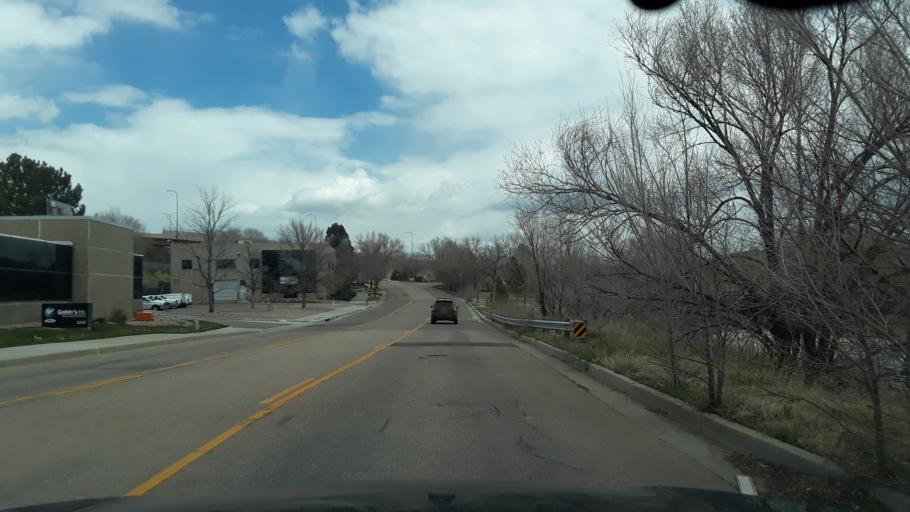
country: US
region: Colorado
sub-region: El Paso County
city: Colorado Springs
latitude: 38.9072
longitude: -104.8238
